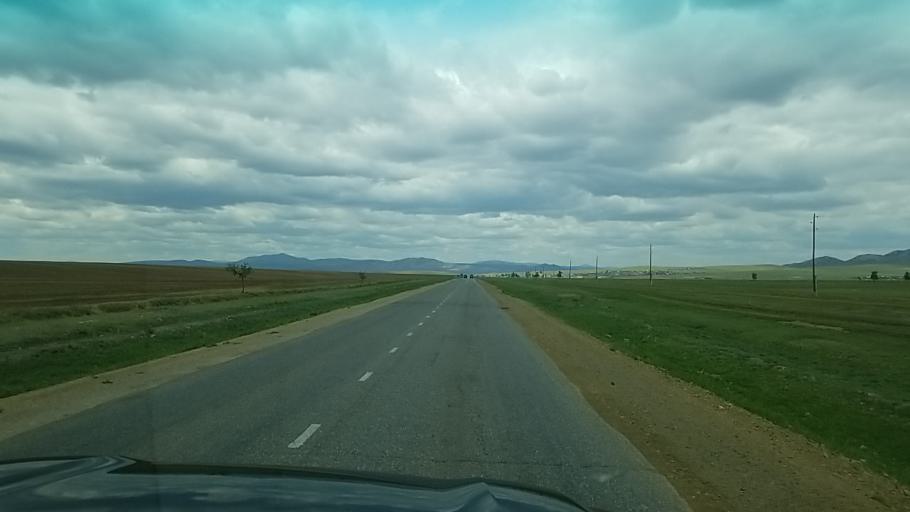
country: MN
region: Darhan Uul
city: Hongor
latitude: 49.2907
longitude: 105.9599
